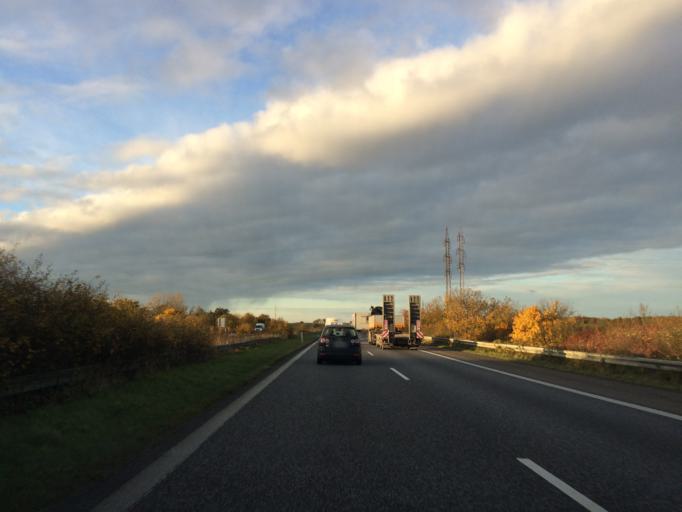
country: DK
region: South Denmark
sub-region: Aabenraa Kommune
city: Rodekro
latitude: 55.0288
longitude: 9.3586
